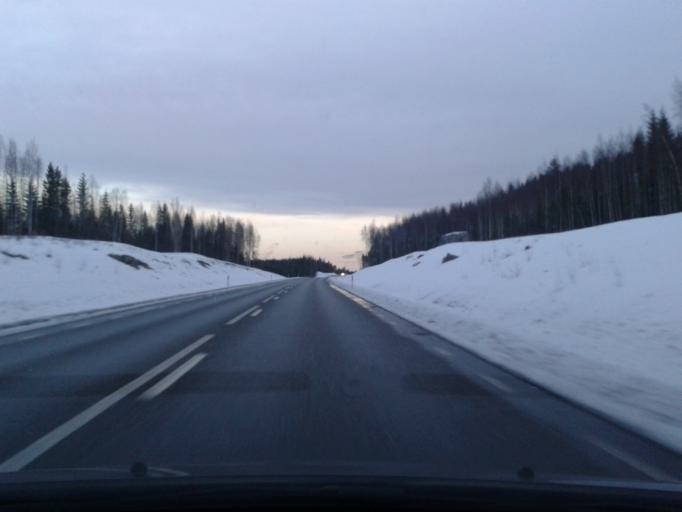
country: SE
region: Vaesternorrland
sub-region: Kramfors Kommun
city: Bollstabruk
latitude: 63.0588
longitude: 17.6058
